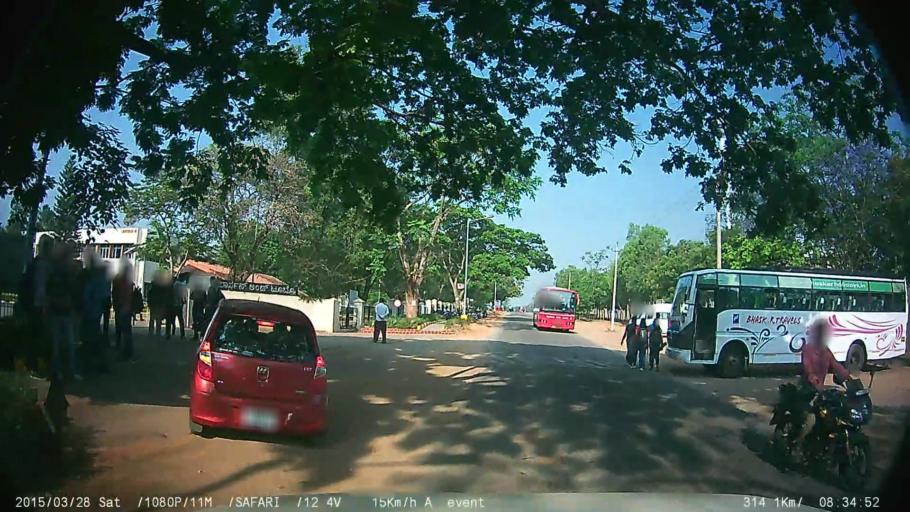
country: IN
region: Karnataka
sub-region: Mysore
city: Mysore
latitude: 12.3574
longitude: 76.5928
